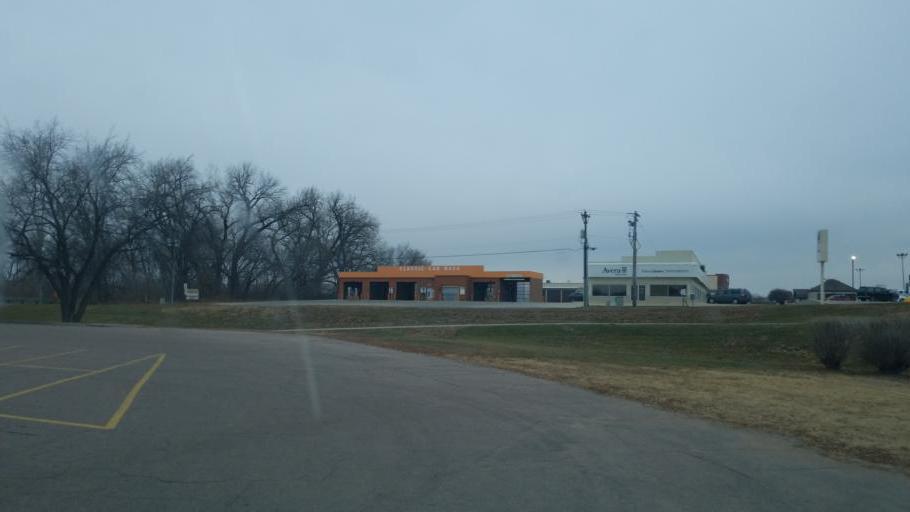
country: US
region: South Dakota
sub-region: Yankton County
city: Yankton
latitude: 42.8937
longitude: -97.3988
